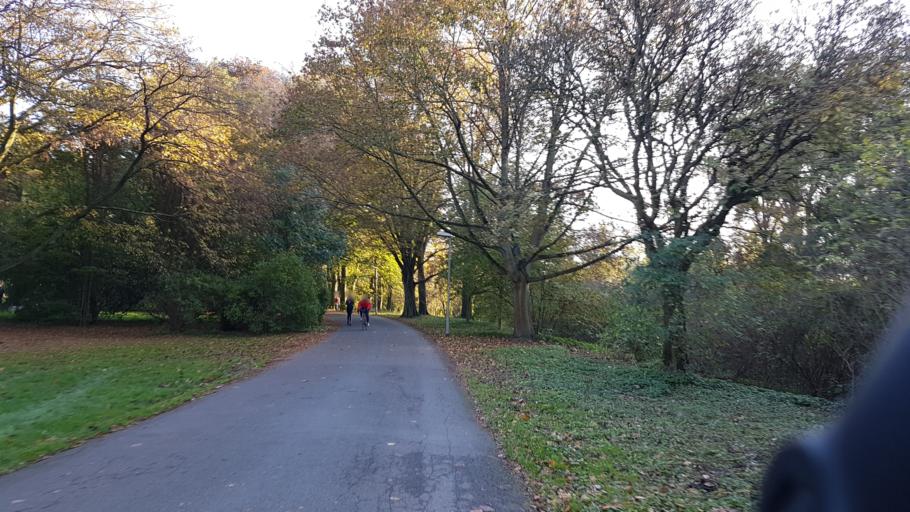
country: DE
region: Lower Saxony
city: Hannover
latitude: 52.3594
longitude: 9.7357
